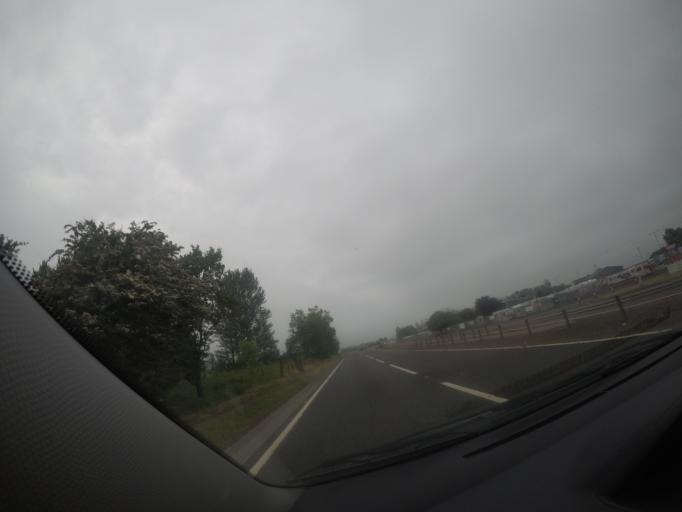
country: GB
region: Scotland
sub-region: Perth and Kinross
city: Errol
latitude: 56.4236
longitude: -3.2232
